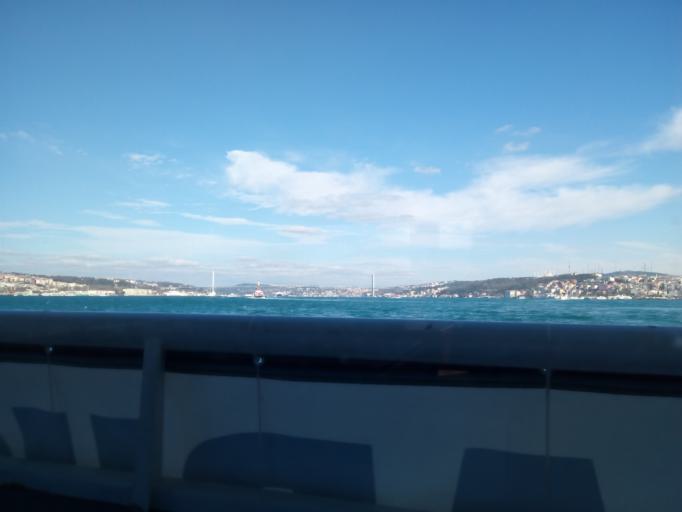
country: TR
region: Istanbul
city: Eminoenue
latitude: 41.0284
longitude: 28.9965
